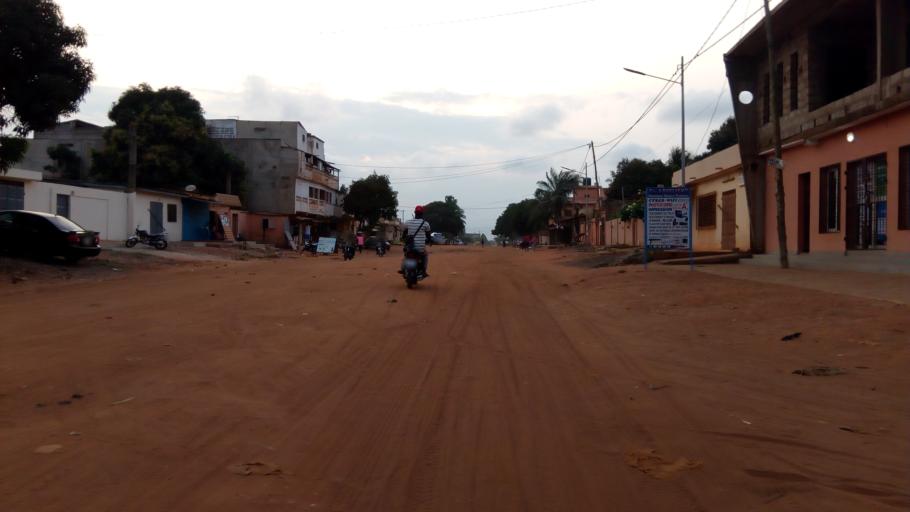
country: TG
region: Maritime
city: Lome
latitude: 6.2320
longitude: 1.1921
